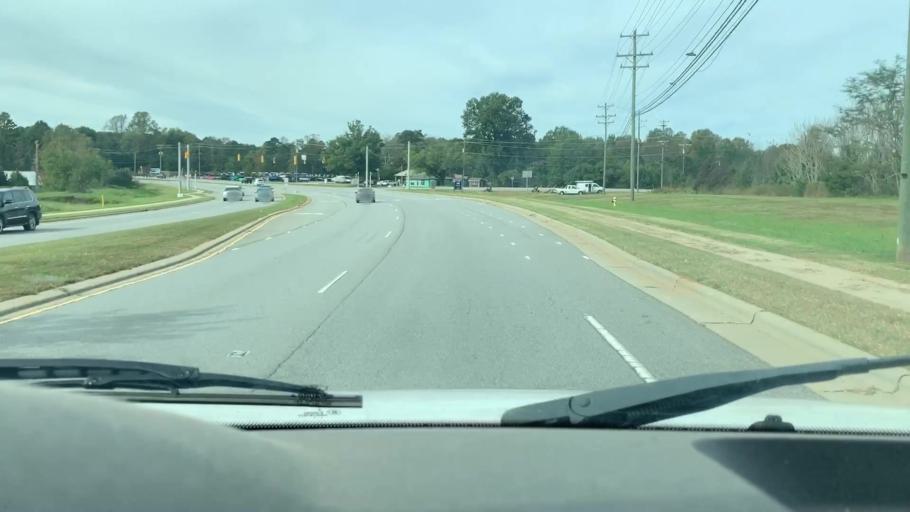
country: US
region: North Carolina
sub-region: Catawba County
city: Lake Norman of Catawba
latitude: 35.5691
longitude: -80.9047
